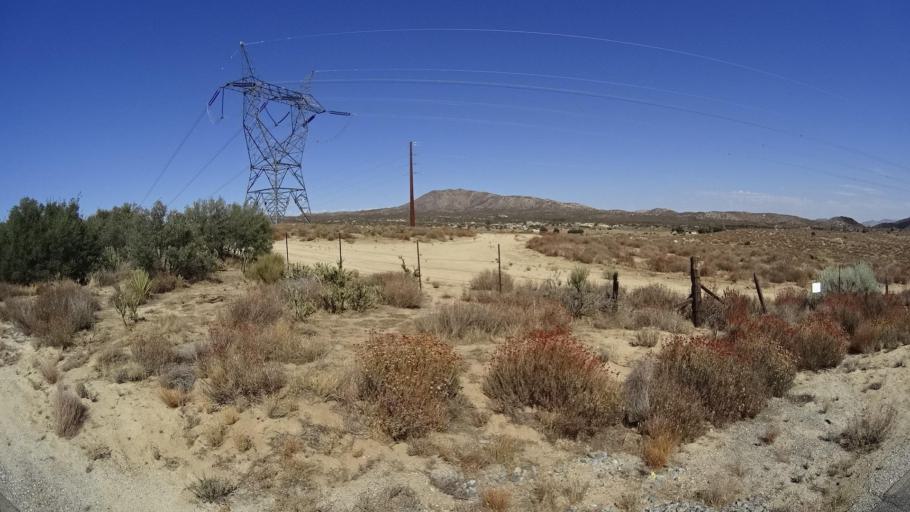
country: MX
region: Baja California
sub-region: Tecate
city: Cereso del Hongo
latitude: 32.6804
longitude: -116.2599
